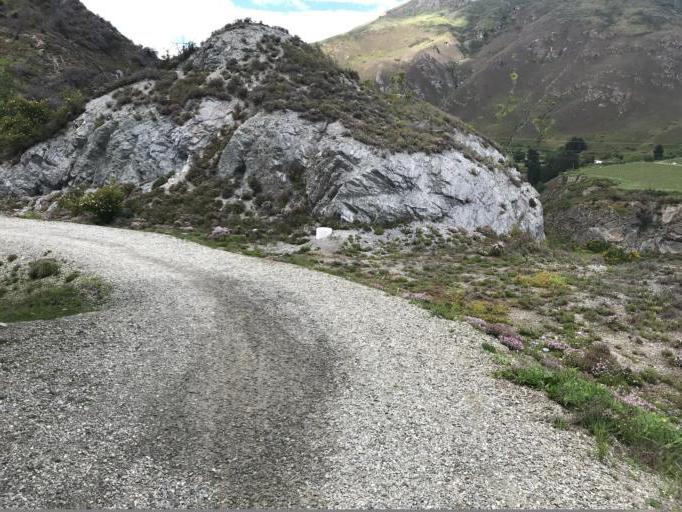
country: NZ
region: Otago
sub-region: Queenstown-Lakes District
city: Arrowtown
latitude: -45.0044
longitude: 168.8798
